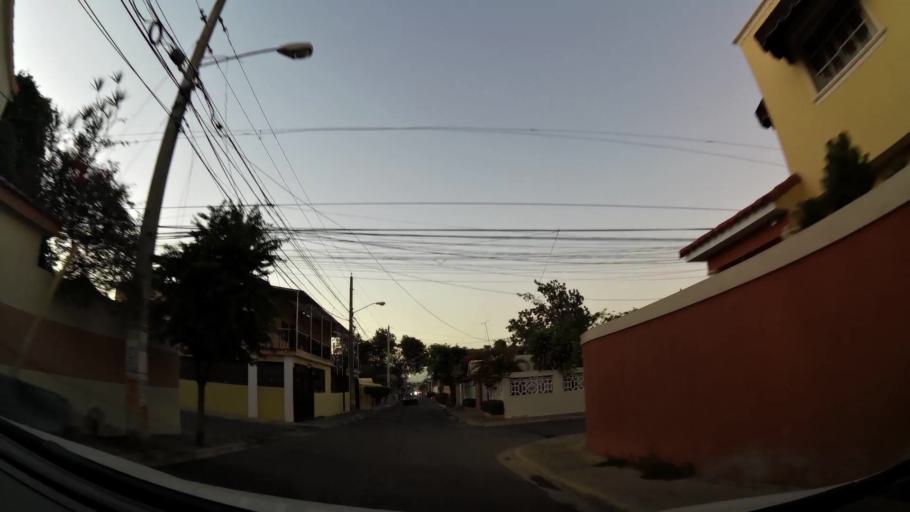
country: DO
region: Santo Domingo
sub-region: Santo Domingo
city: Santo Domingo Este
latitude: 18.4908
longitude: -69.8389
